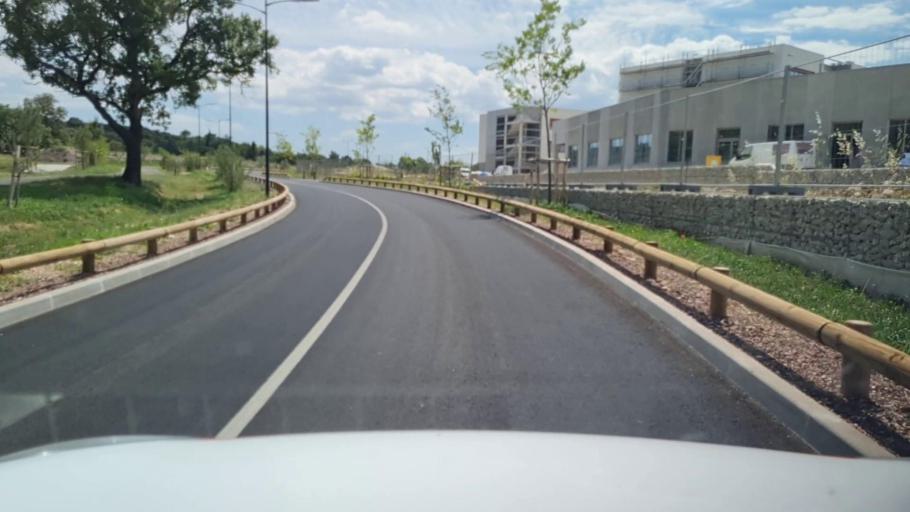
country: FR
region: Languedoc-Roussillon
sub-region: Departement de l'Herault
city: Boisseron
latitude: 43.7766
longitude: 4.0706
